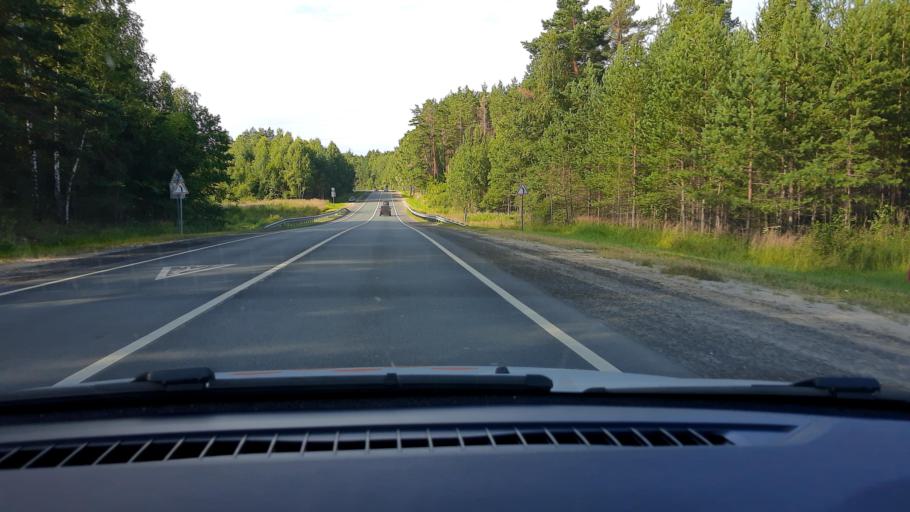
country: RU
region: Nizjnij Novgorod
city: Arzamas
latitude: 55.5138
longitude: 43.9013
